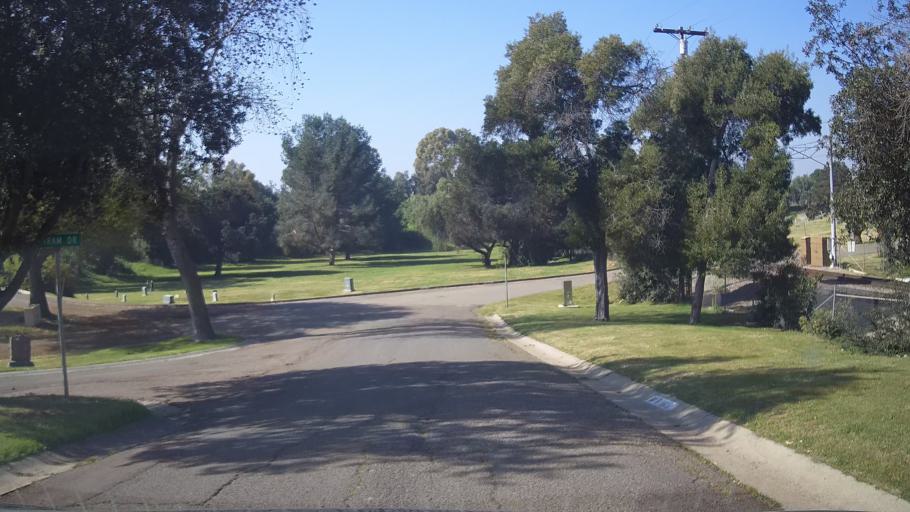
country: US
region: California
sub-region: San Diego County
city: National City
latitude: 32.7067
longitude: -117.1136
